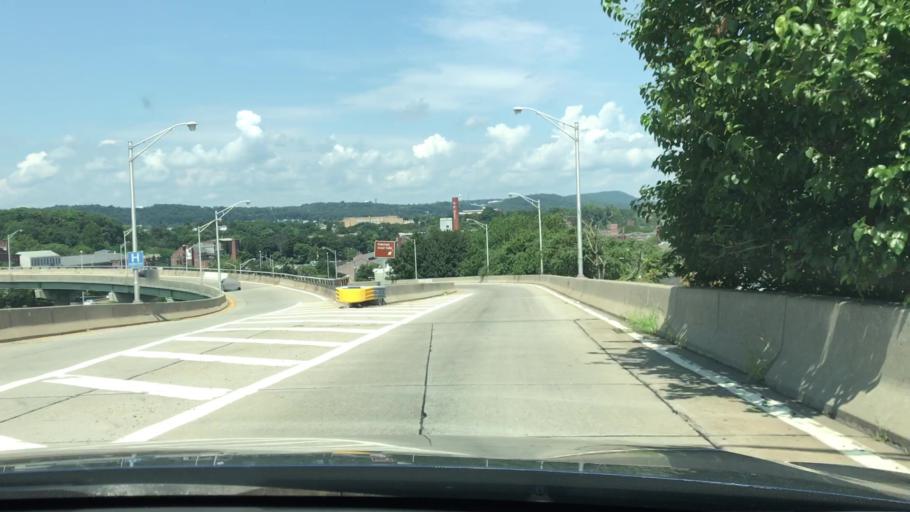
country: US
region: New Jersey
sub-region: Passaic County
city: Paterson
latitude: 40.9096
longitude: -74.1743
